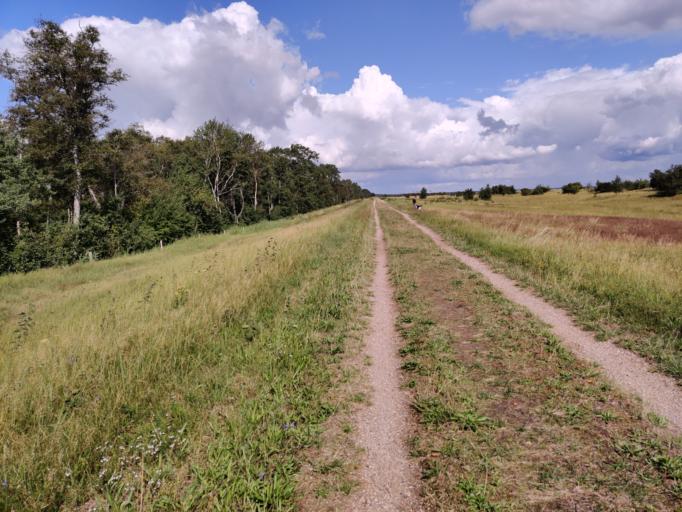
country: DK
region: Zealand
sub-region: Guldborgsund Kommune
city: Nykobing Falster
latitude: 54.6274
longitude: 11.9621
